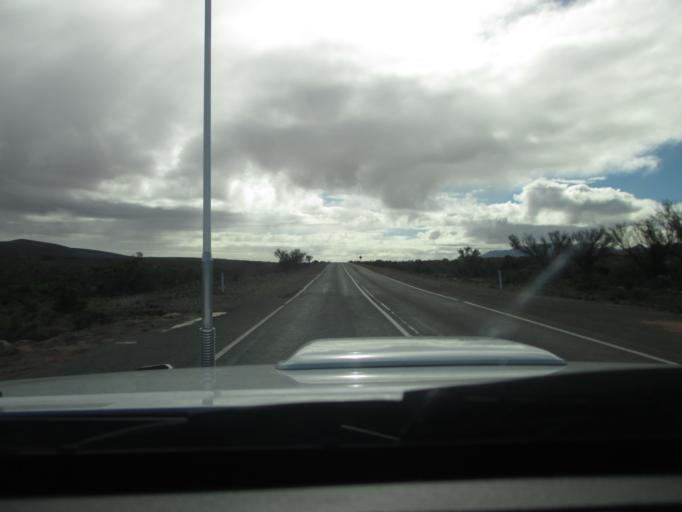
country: AU
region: South Australia
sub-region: Flinders Ranges
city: Quorn
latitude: -31.6474
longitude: 138.3812
